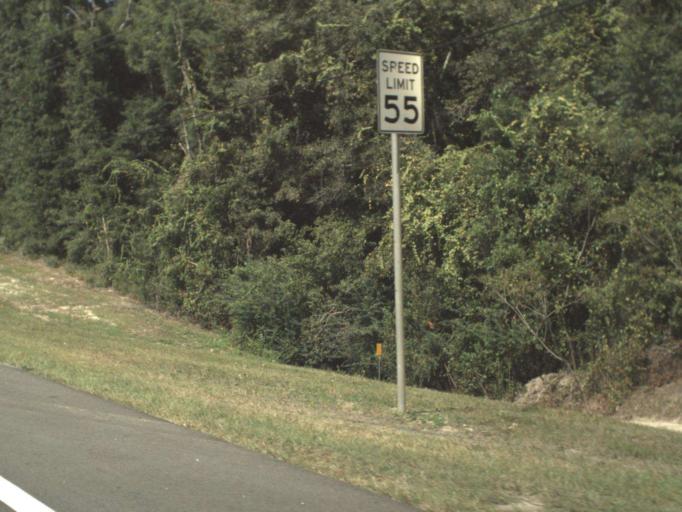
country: US
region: Florida
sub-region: Walton County
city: Freeport
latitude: 30.5037
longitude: -86.1516
